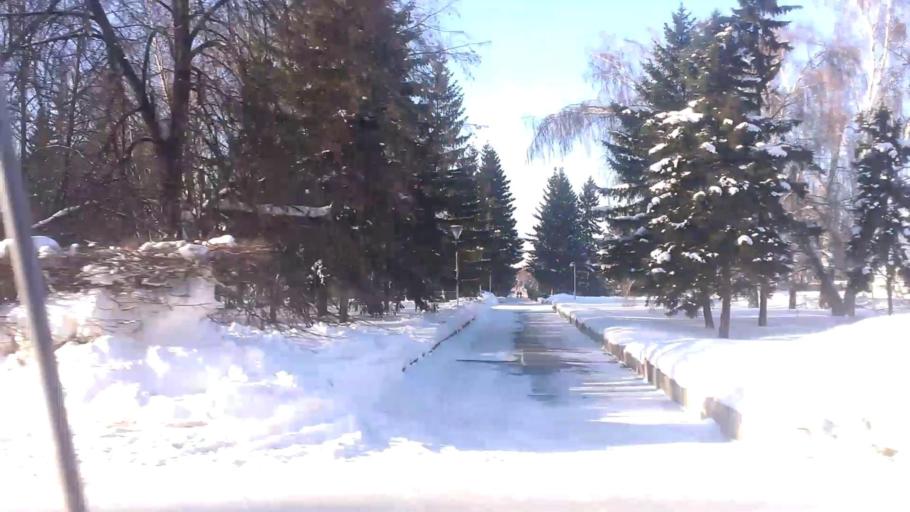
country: RU
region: Altai Krai
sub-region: Gorod Barnaulskiy
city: Barnaul
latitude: 53.3493
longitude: 83.7615
